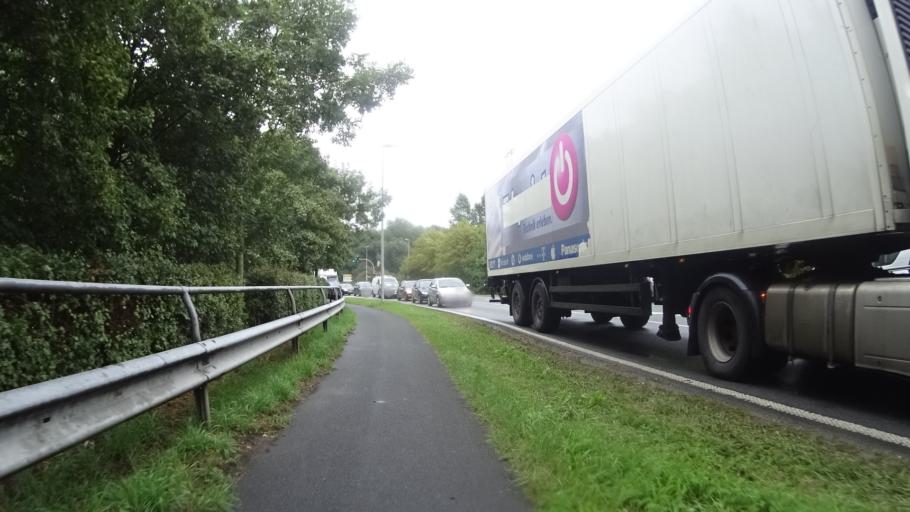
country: DE
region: Lower Saxony
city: Leer
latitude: 53.2170
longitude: 7.4319
